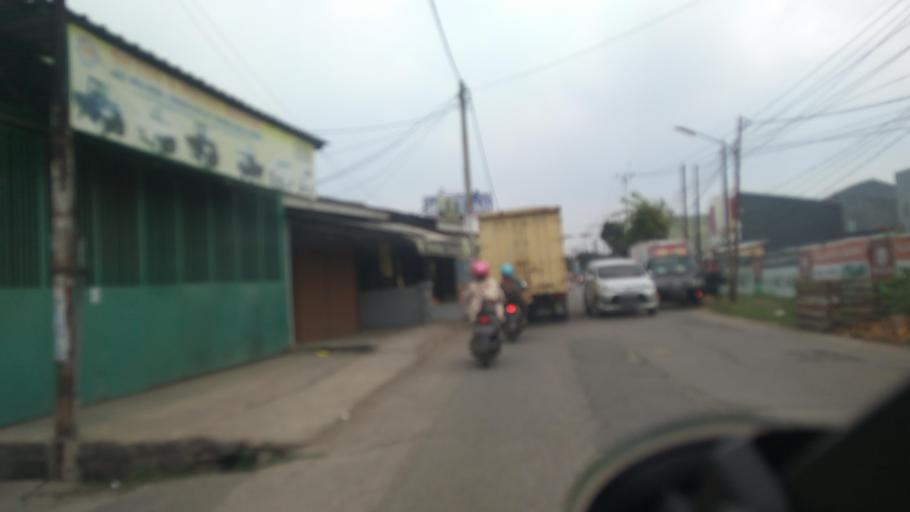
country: ID
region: West Java
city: Bekasi
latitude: -6.2003
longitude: 107.0377
